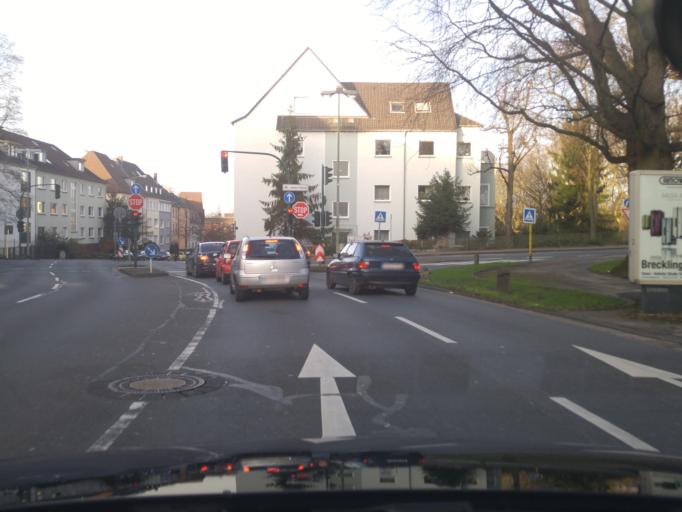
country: DE
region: North Rhine-Westphalia
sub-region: Regierungsbezirk Dusseldorf
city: Essen
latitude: 51.4431
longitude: 7.0225
